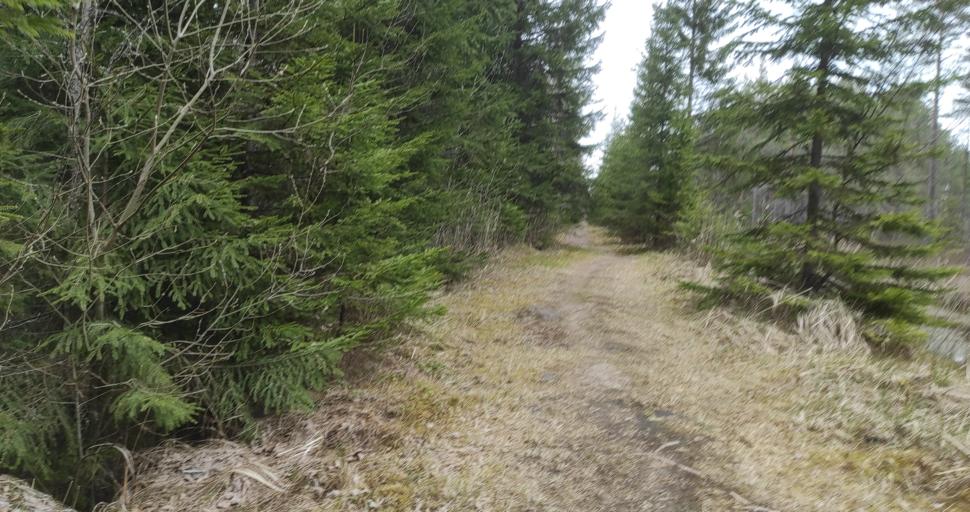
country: LV
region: Dundaga
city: Dundaga
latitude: 57.3450
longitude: 22.1497
